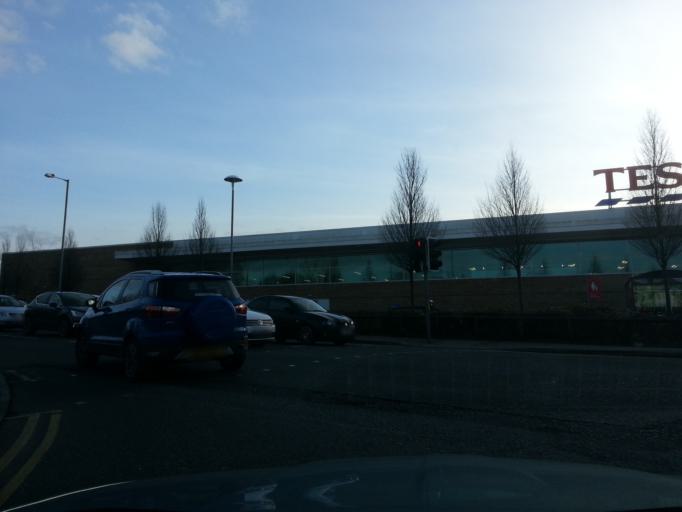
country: GB
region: Northern Ireland
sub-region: Fermanagh District
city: Enniskillen
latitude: 54.3420
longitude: -7.6272
